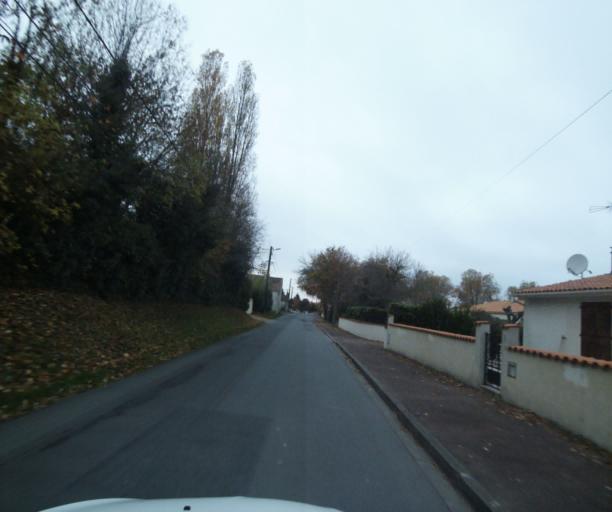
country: FR
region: Poitou-Charentes
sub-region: Departement de la Charente-Maritime
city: Fontcouverte
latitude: 45.7433
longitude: -0.6037
